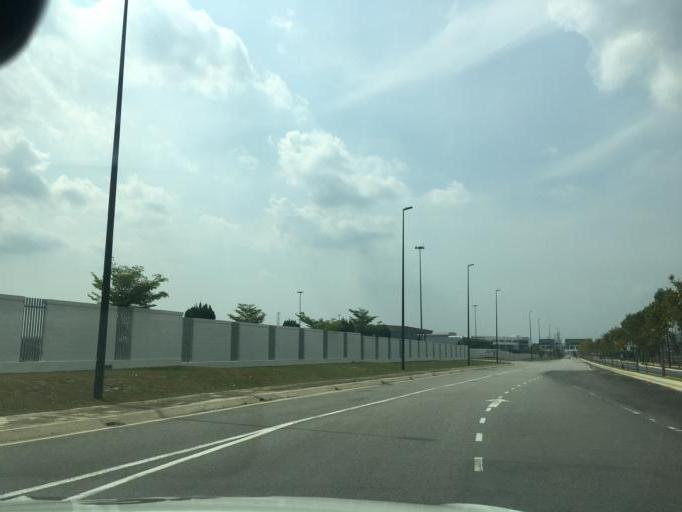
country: MY
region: Selangor
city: Klang
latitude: 3.0805
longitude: 101.4765
